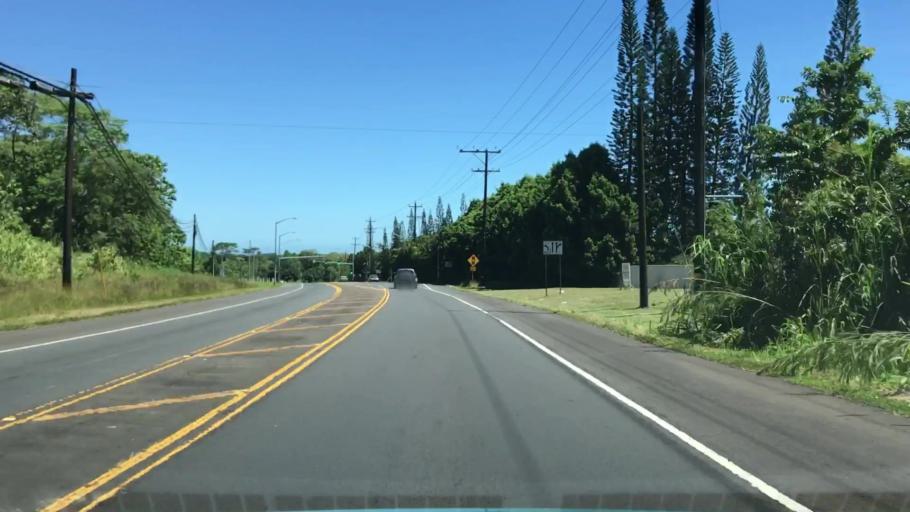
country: US
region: Hawaii
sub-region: Hawaii County
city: Kurtistown
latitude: 19.6091
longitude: -155.0485
